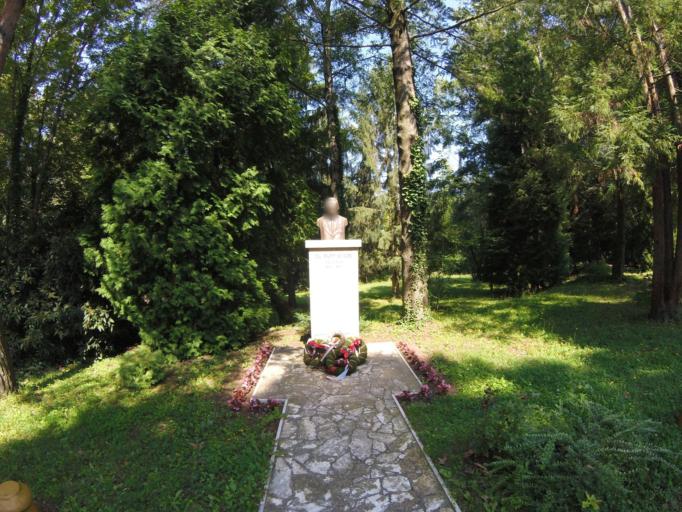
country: HU
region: Zala
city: Becsehely
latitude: 46.5199
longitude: 16.7355
